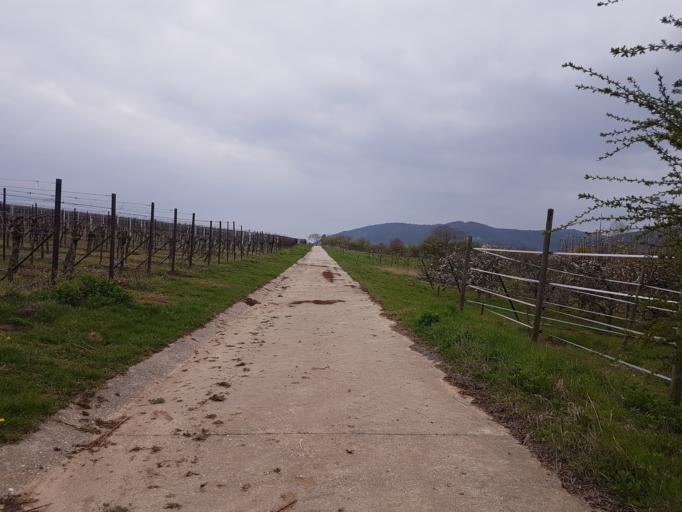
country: DE
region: Rheinland-Pfalz
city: Bochingen
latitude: 49.2286
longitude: 8.0849
